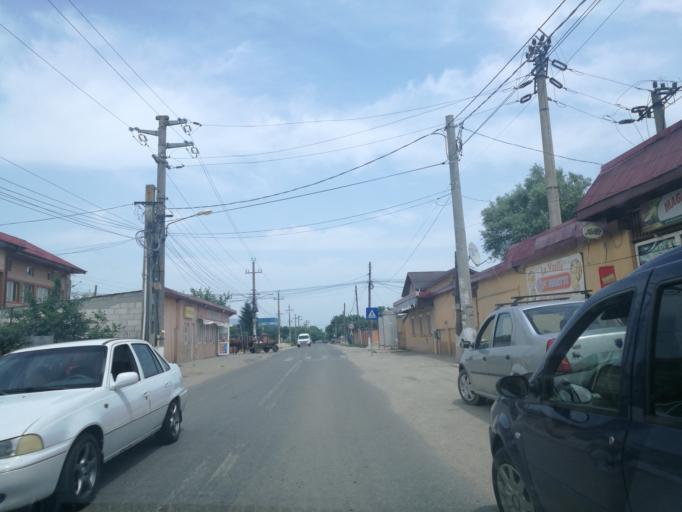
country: RO
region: Ilfov
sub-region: Comuna Vidra
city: Vidra
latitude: 44.2638
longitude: 26.1657
